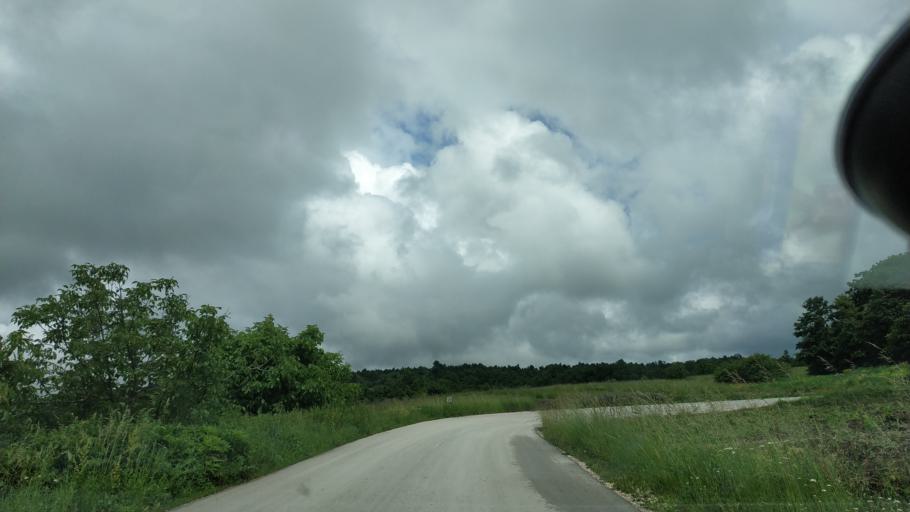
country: RS
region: Central Serbia
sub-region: Zajecarski Okrug
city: Soko Banja
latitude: 43.6868
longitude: 21.9304
